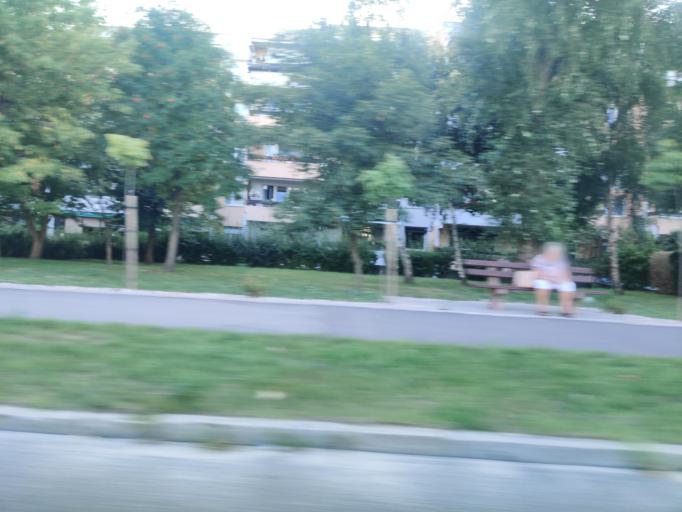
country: PL
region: Greater Poland Voivodeship
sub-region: Konin
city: Konin
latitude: 52.2334
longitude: 18.2602
